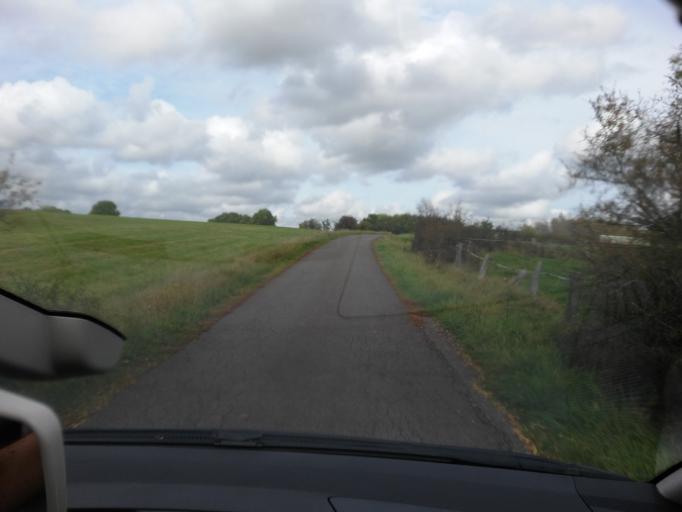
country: BE
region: Wallonia
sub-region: Province du Luxembourg
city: Arlon
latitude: 49.6383
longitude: 5.7799
